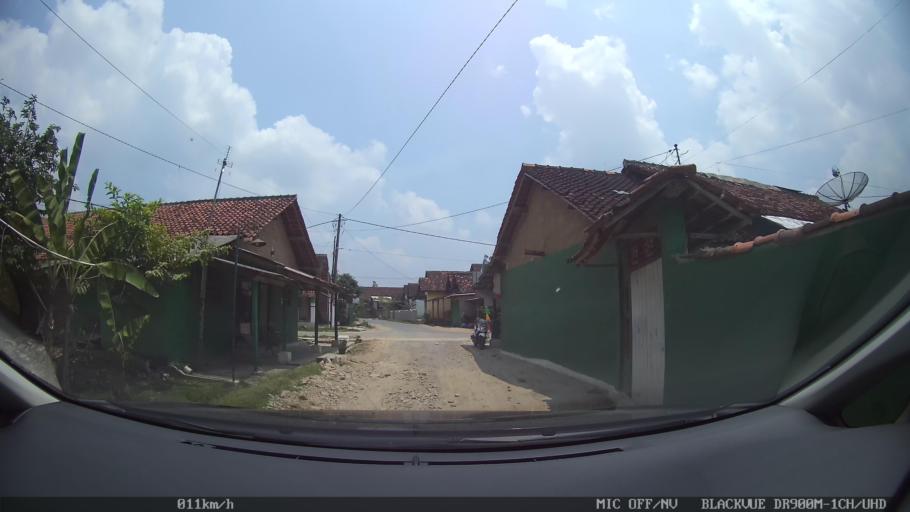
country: ID
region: Lampung
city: Pringsewu
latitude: -5.3495
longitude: 104.9885
